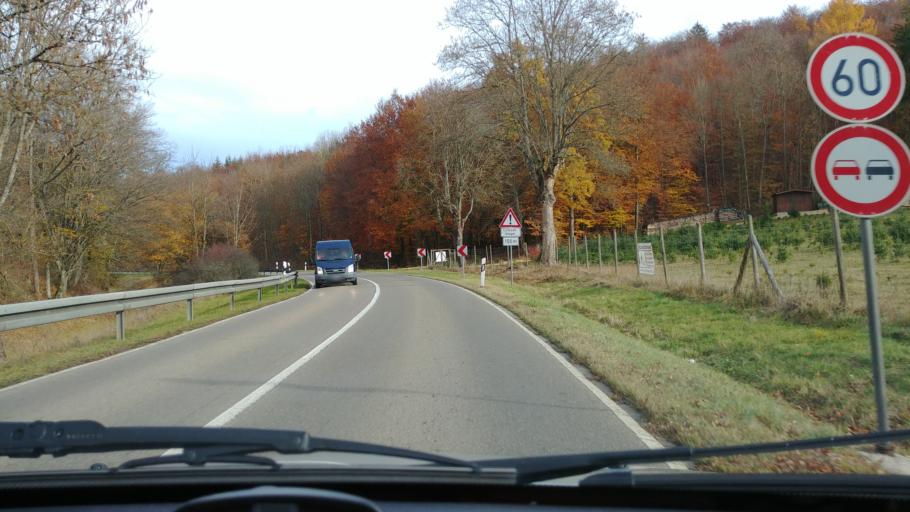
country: DE
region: Baden-Wuerttemberg
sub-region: Regierungsbezirk Stuttgart
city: Heidenheim an der Brenz
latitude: 48.6666
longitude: 10.1873
